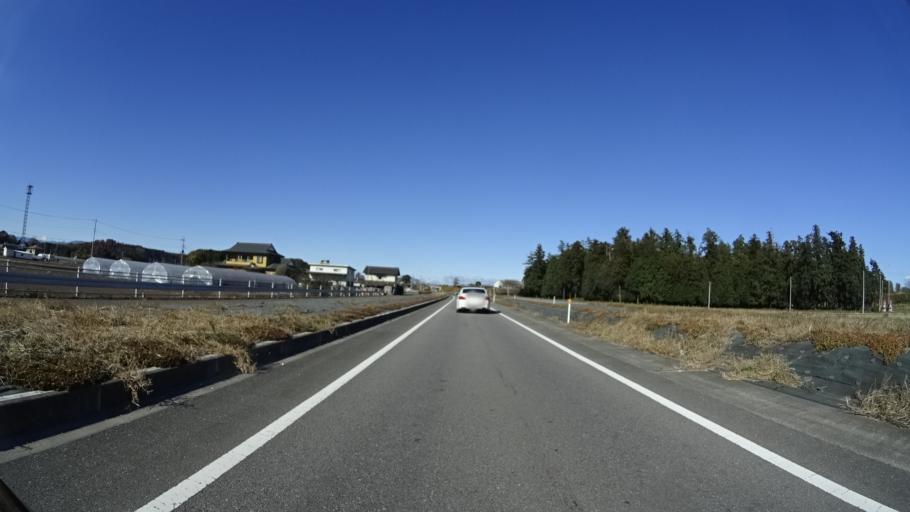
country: JP
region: Tochigi
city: Kanuma
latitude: 36.4881
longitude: 139.7533
